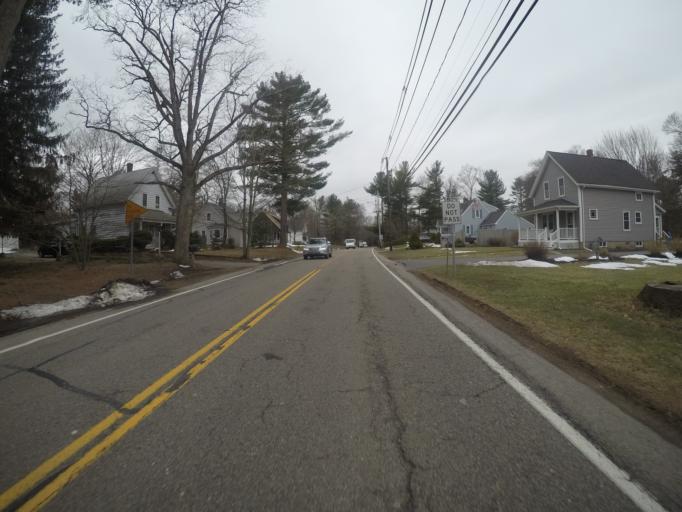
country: US
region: Massachusetts
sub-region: Bristol County
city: Easton
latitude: 42.0403
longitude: -71.0882
